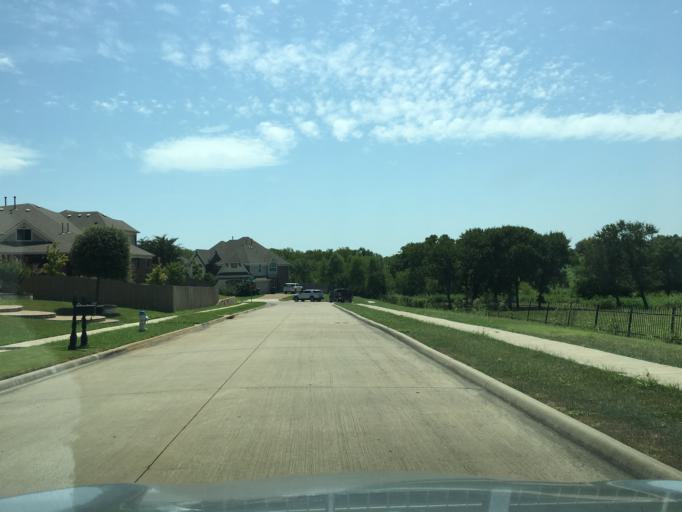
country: US
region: Texas
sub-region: Dallas County
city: Rowlett
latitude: 32.8860
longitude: -96.6007
